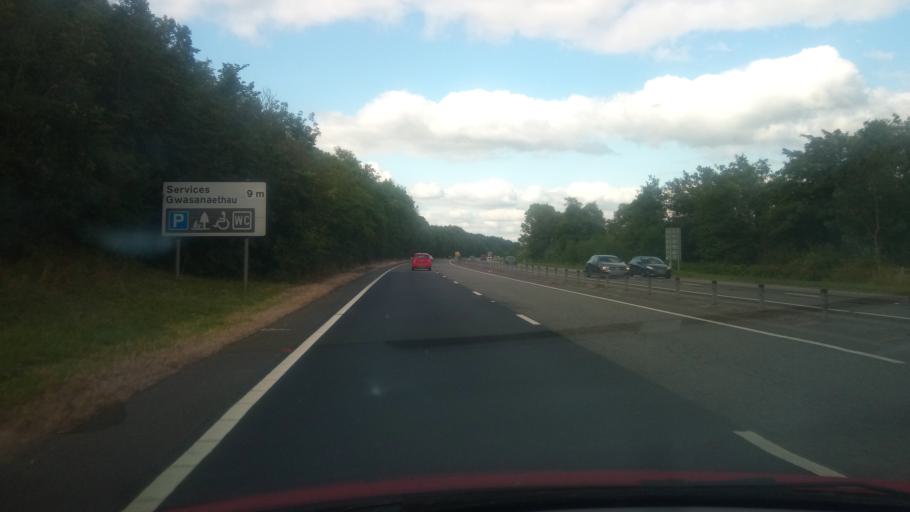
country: GB
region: Wales
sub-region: Monmouthshire
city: Llangwm
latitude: 51.7166
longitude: -2.8611
